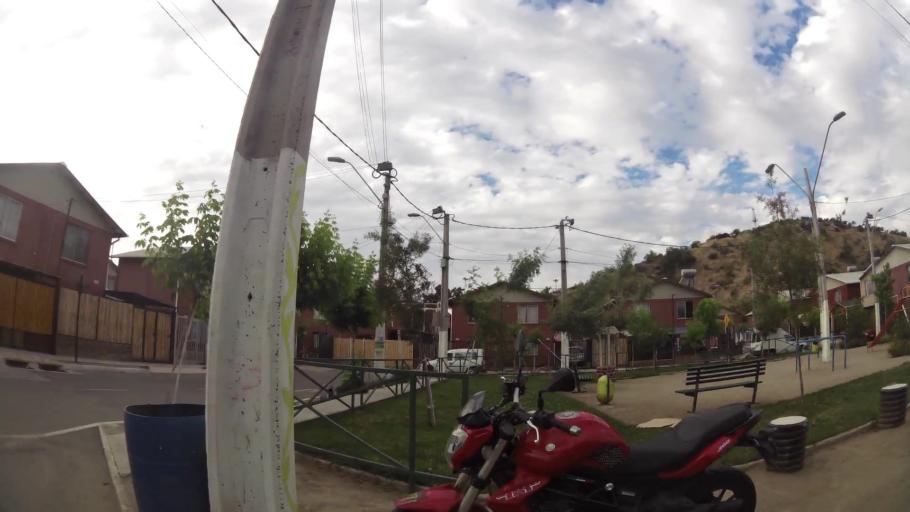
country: CL
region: Santiago Metropolitan
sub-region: Provincia de Cordillera
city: Puente Alto
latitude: -33.6284
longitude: -70.6049
